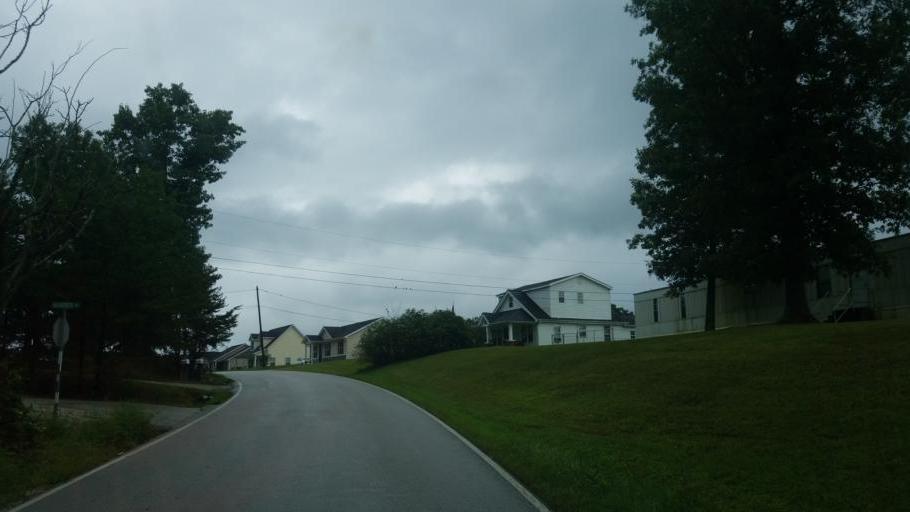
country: US
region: Kentucky
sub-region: Rowan County
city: Morehead
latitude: 38.1511
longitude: -83.5091
